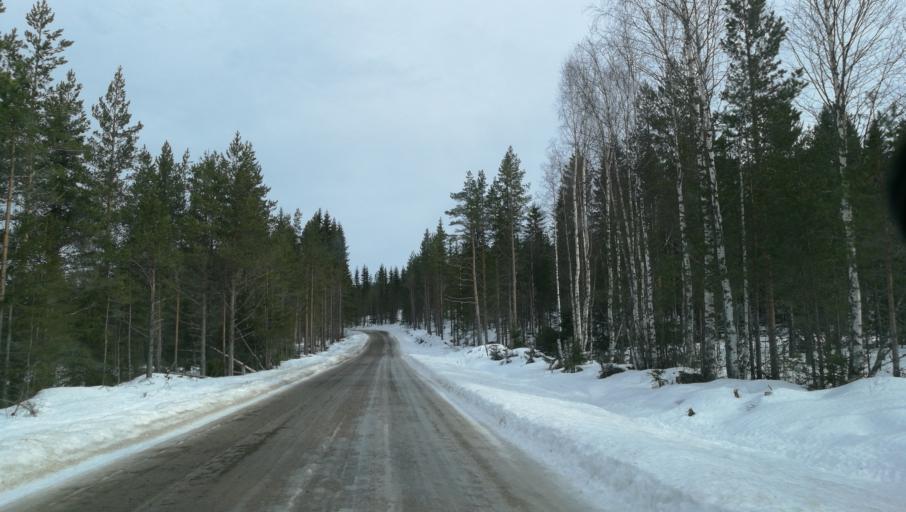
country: SE
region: Vaermland
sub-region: Torsby Kommun
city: Torsby
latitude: 60.6494
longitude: 12.8000
